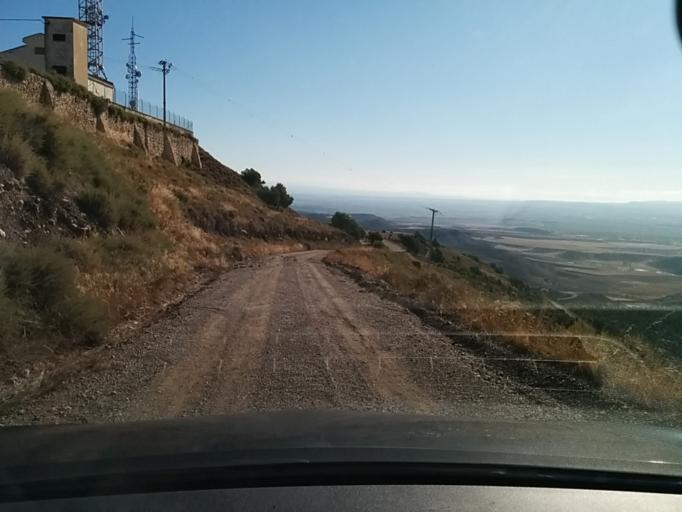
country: ES
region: Aragon
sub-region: Provincia de Zaragoza
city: Novillas
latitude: 42.0199
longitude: -1.3244
